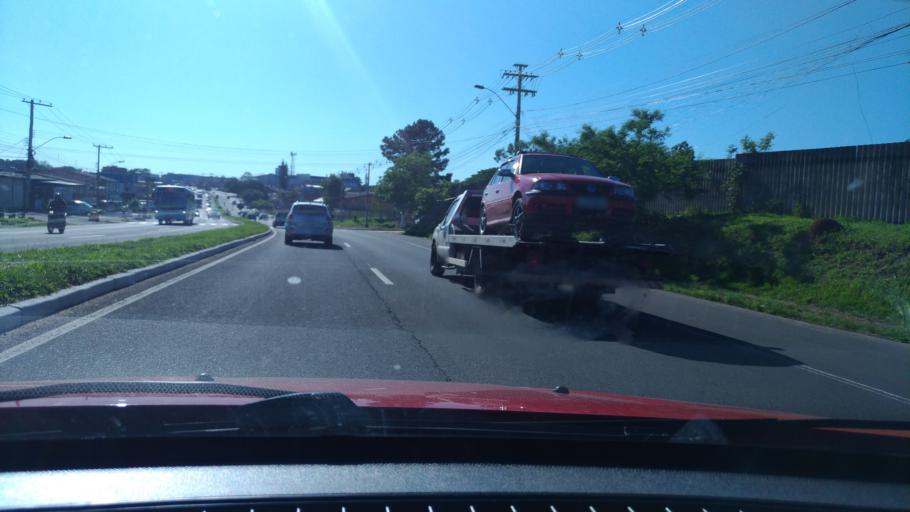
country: BR
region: Rio Grande do Sul
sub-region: Viamao
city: Viamao
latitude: -30.0928
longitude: -51.0703
